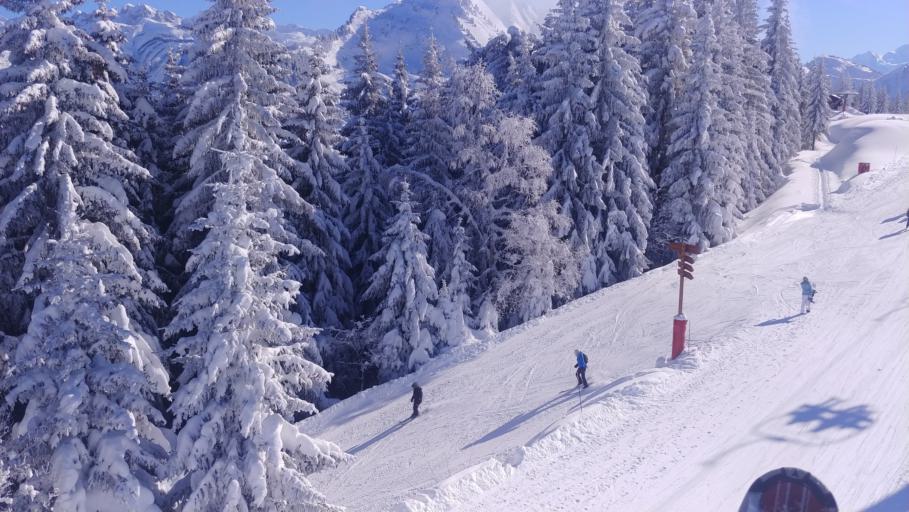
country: FR
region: Rhone-Alpes
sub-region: Departement de la Haute-Savoie
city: Morzine
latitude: 46.1646
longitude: 6.6929
